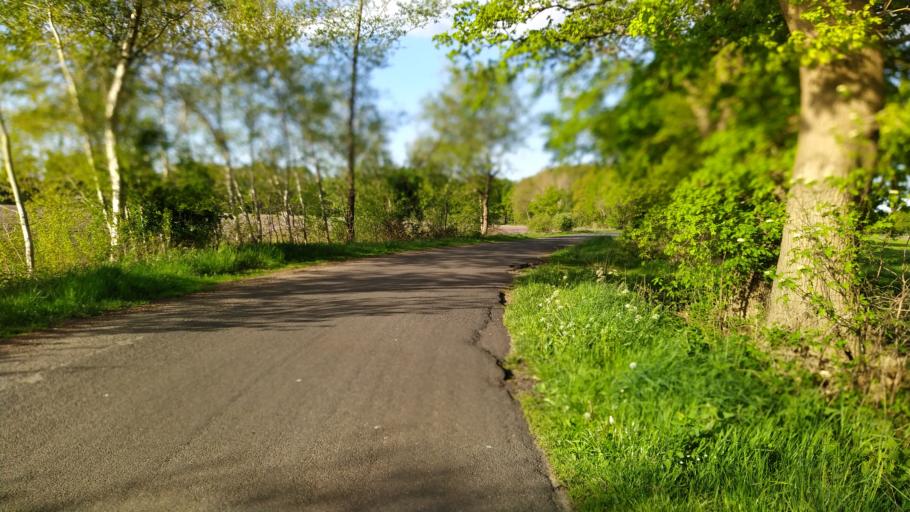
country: DE
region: Lower Saxony
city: Farven
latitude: 53.4251
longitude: 9.3394
